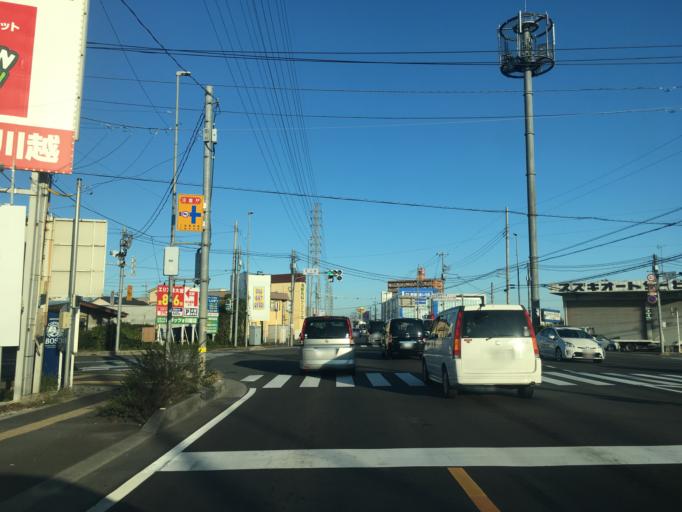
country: JP
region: Saitama
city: Kawagoe
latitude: 35.9285
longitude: 139.4914
